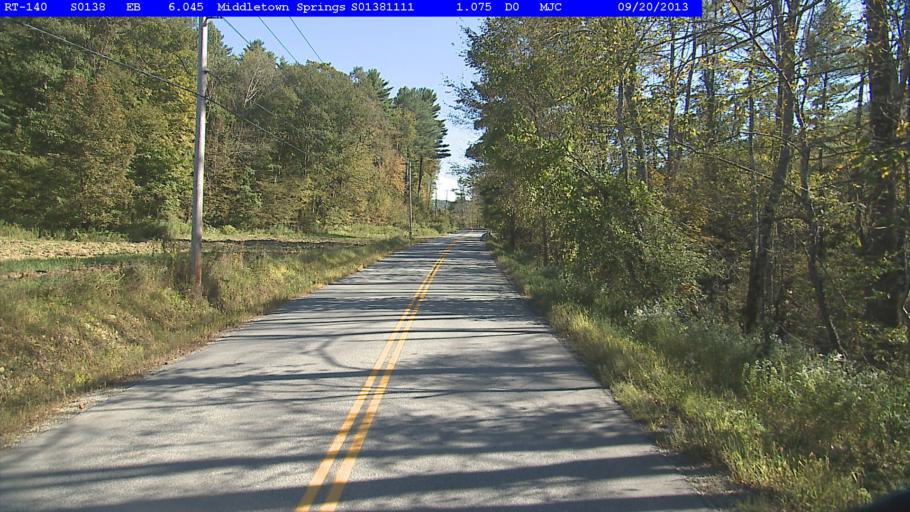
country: US
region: Vermont
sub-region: Rutland County
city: Poultney
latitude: 43.4914
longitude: -73.1544
